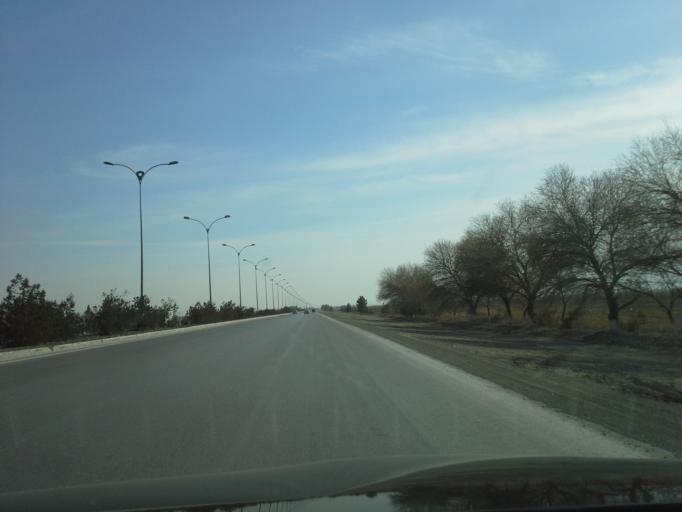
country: TM
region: Ahal
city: Abadan
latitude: 38.1305
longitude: 58.0230
